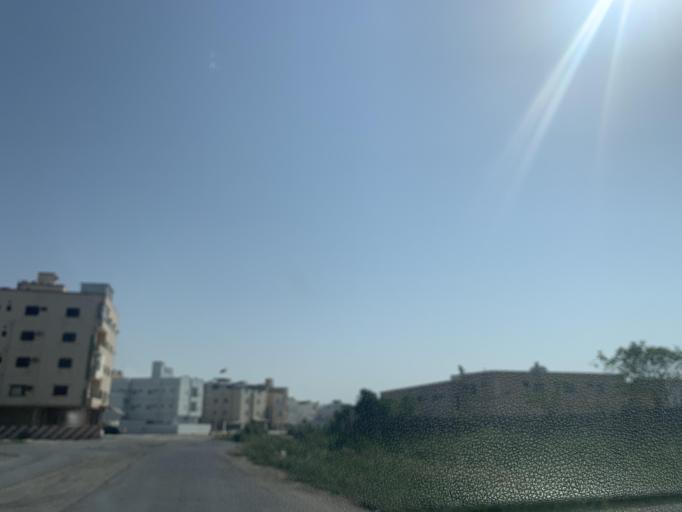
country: BH
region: Central Governorate
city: Madinat Hamad
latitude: 26.1367
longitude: 50.4865
